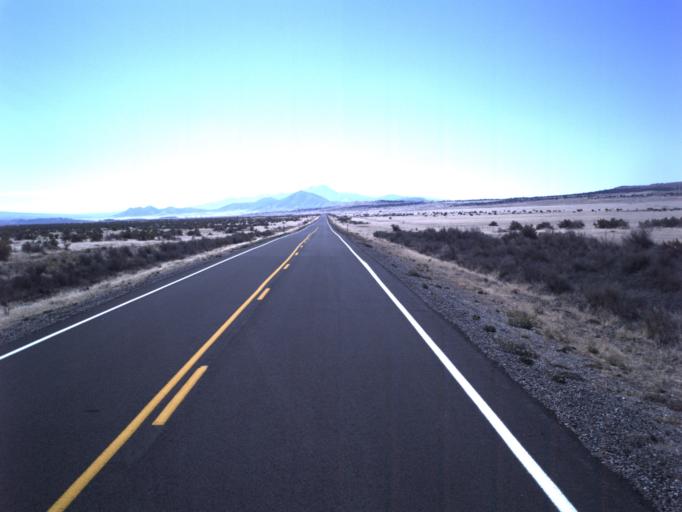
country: US
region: Utah
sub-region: Tooele County
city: Grantsville
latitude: 40.2869
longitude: -112.7421
